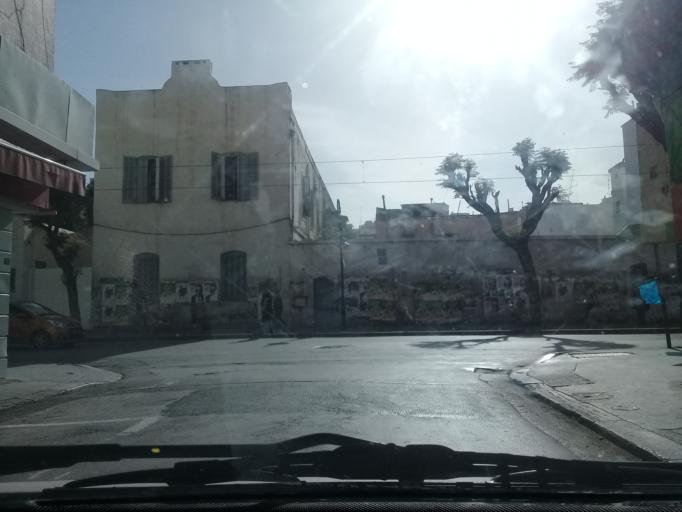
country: TN
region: Tunis
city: Tunis
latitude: 36.8029
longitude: 10.1813
